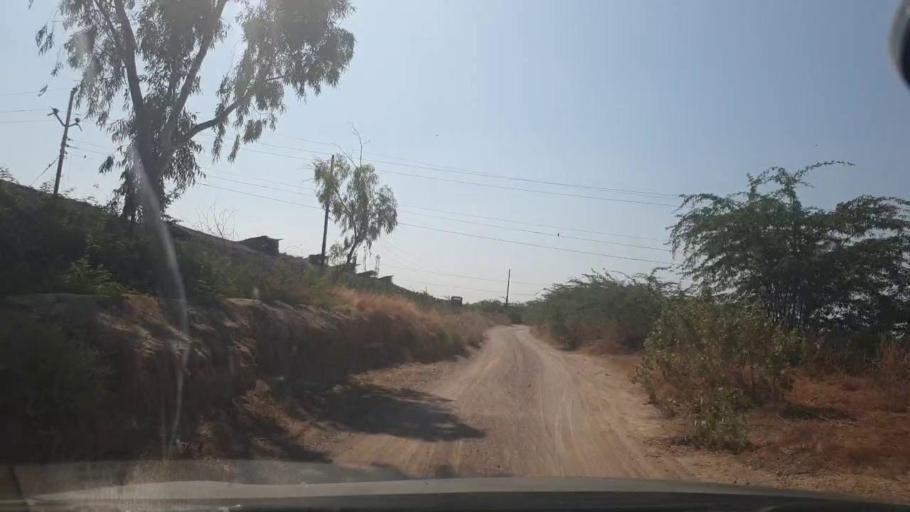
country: PK
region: Sindh
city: Malir Cantonment
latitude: 25.1674
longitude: 67.2046
